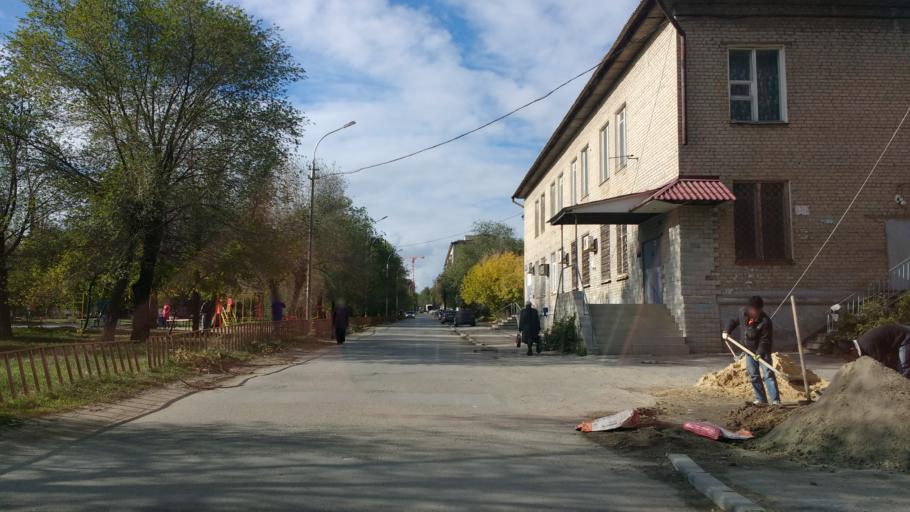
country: RU
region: Volgograd
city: Krasnoslobodsk
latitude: 48.7683
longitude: 44.5541
